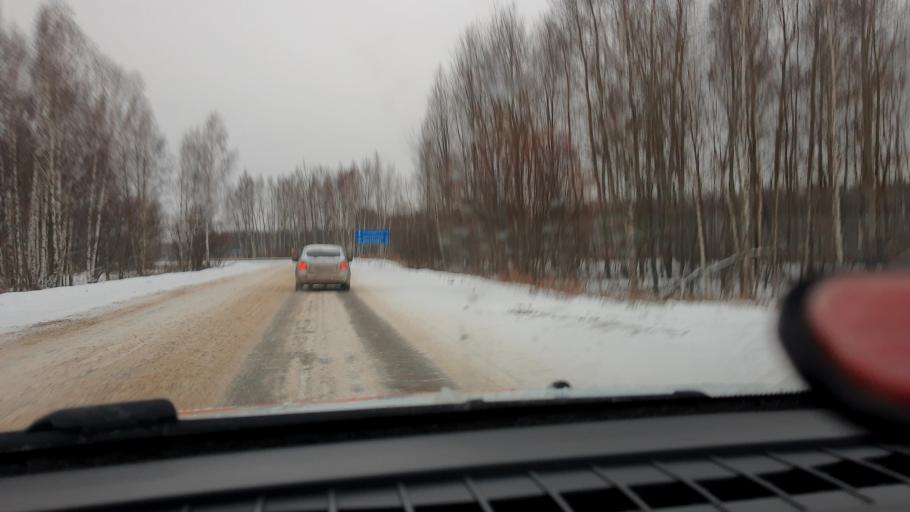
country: RU
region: Nizjnij Novgorod
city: Pamyat' Parizhskoy Kommuny
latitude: 56.2435
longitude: 44.4950
